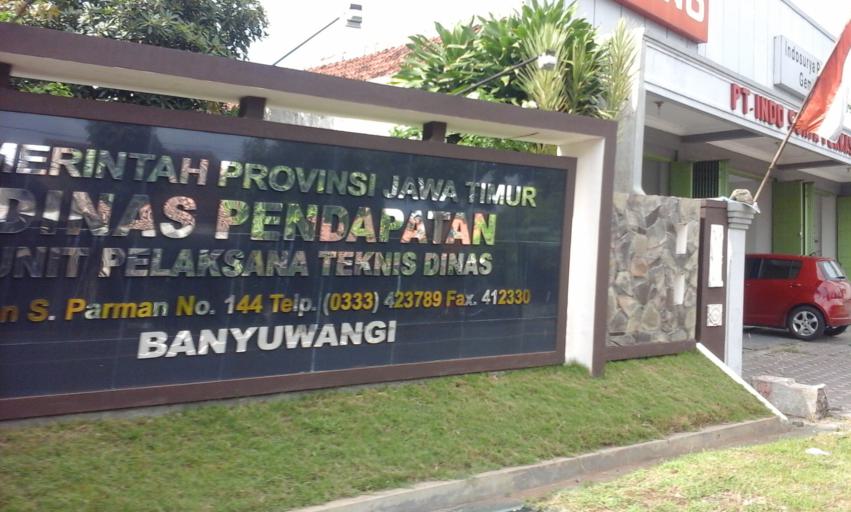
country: ID
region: East Java
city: Krajan
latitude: -8.2456
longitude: 114.3503
